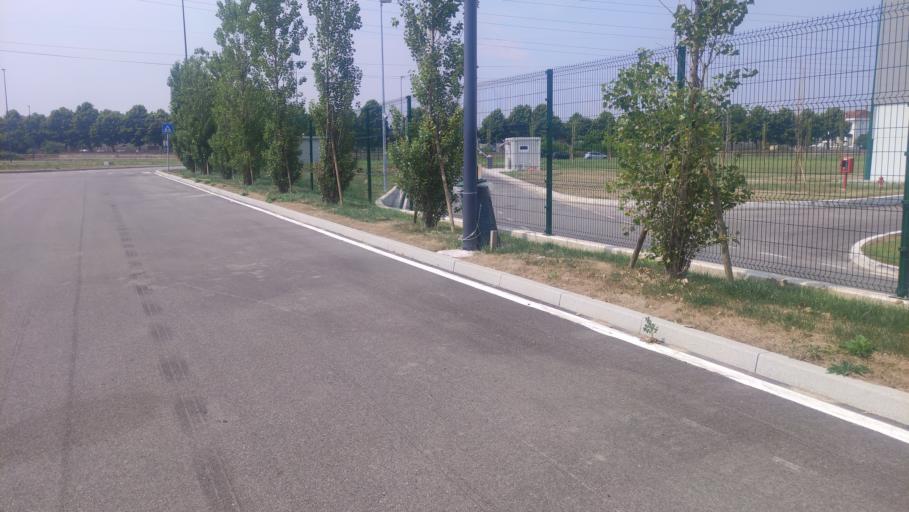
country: IT
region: Emilia-Romagna
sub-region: Provincia di Piacenza
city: Piacenza
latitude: 45.0333
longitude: 9.7414
